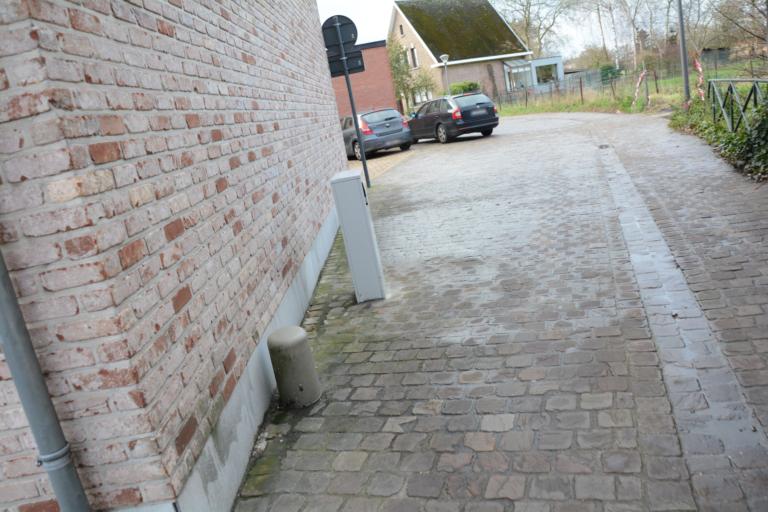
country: BE
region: Flanders
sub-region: Provincie Vlaams-Brabant
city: Londerzeel
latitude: 50.9958
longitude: 4.2661
